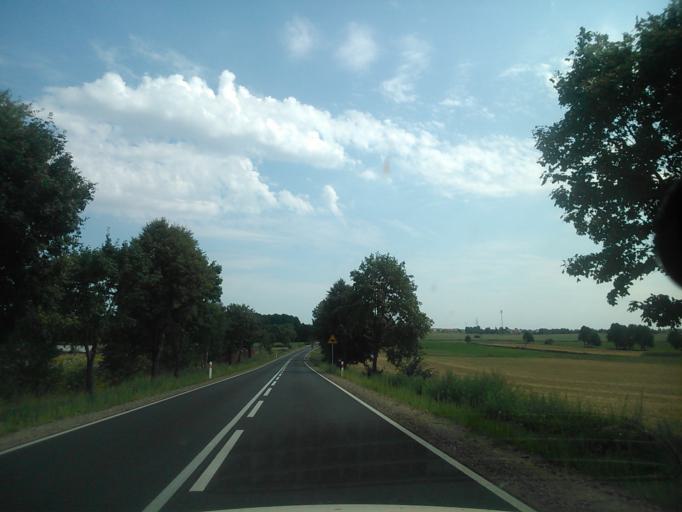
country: PL
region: Warmian-Masurian Voivodeship
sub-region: Powiat dzialdowski
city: Dzialdowo
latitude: 53.2359
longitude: 20.1320
